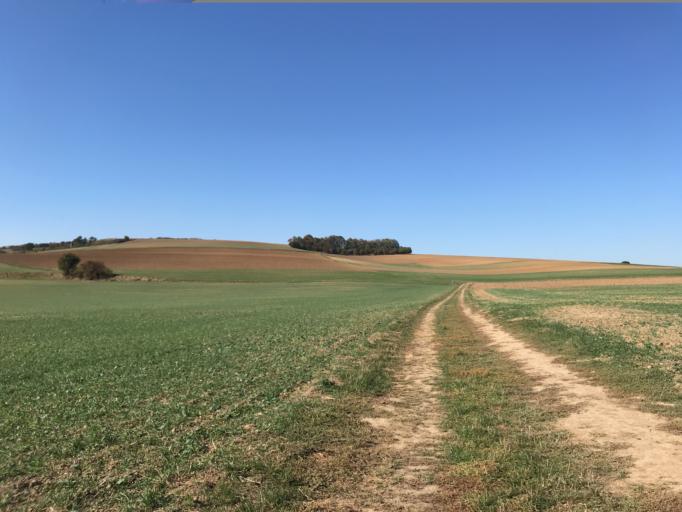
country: DE
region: Rheinland-Pfalz
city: Kobern-Gondorf
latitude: 50.3051
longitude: 7.4331
